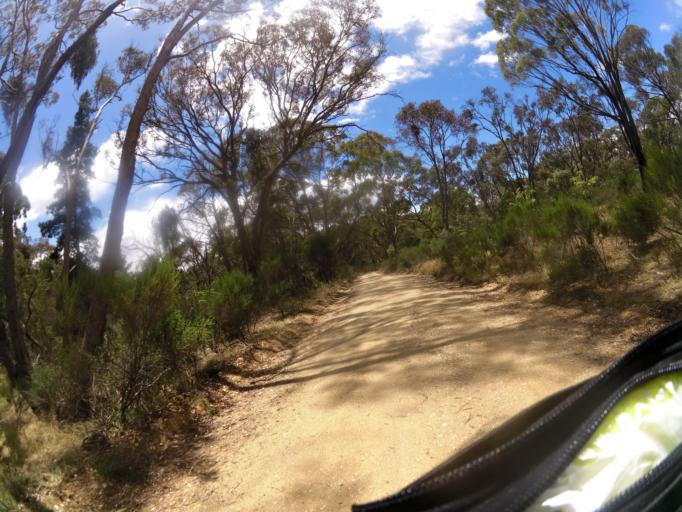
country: AU
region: Victoria
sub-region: Mount Alexander
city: Castlemaine
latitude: -37.0593
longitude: 144.2693
